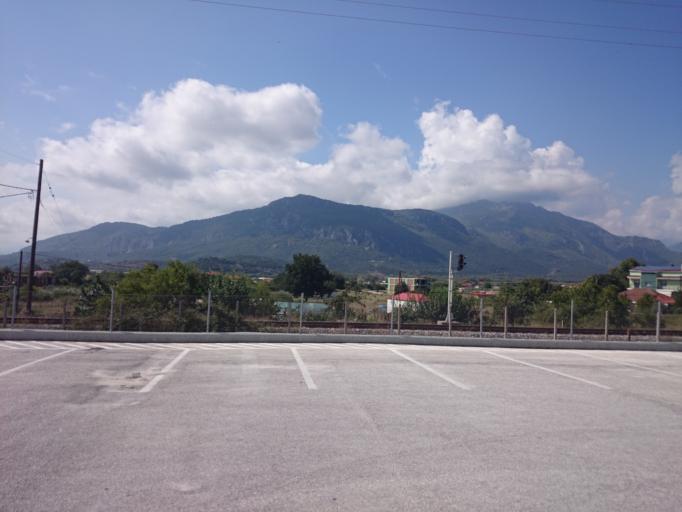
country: GR
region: Thessaly
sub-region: Trikala
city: Kalampaka
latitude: 39.7001
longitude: 21.6357
